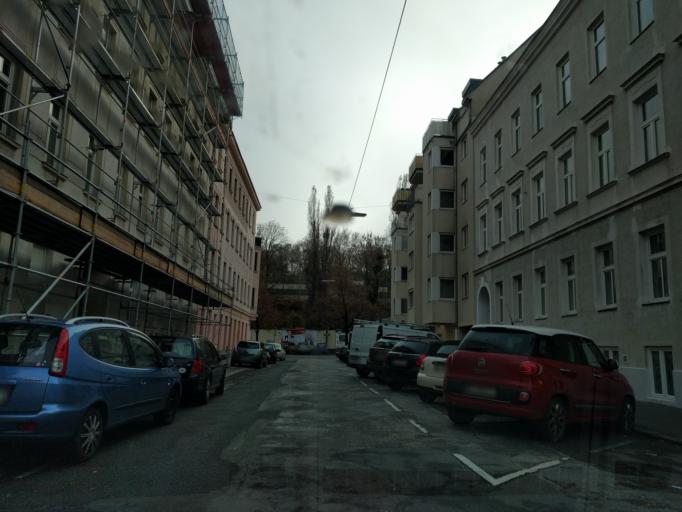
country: AT
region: Vienna
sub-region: Wien Stadt
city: Vienna
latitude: 48.2410
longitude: 16.3366
